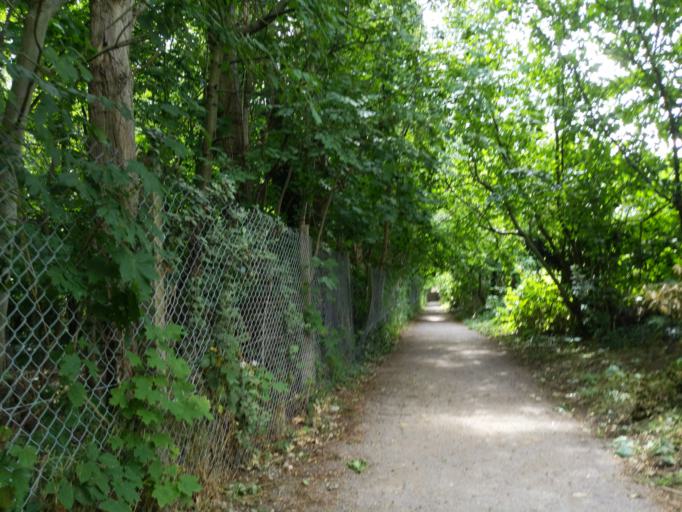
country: GB
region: England
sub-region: Surrey
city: Esher
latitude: 51.3731
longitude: -0.3908
